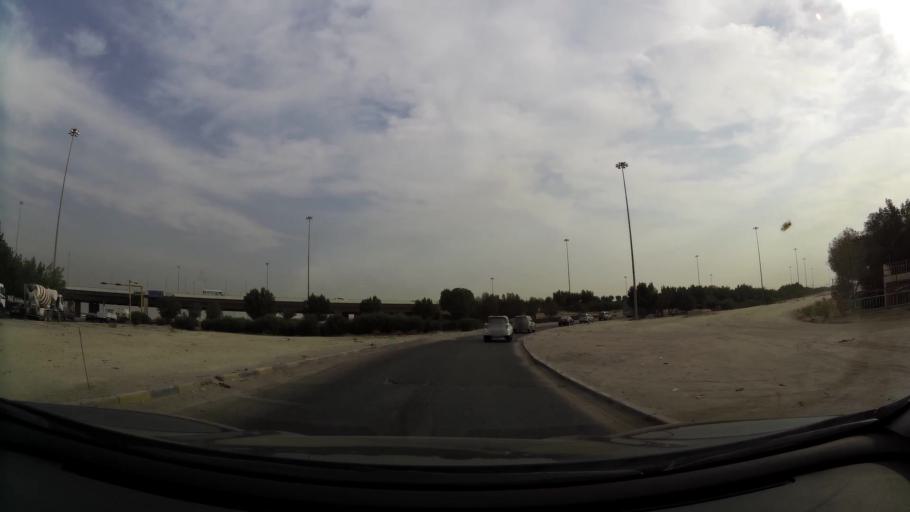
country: KW
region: Muhafazat al Jahra'
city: Al Jahra'
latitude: 29.3223
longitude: 47.7507
